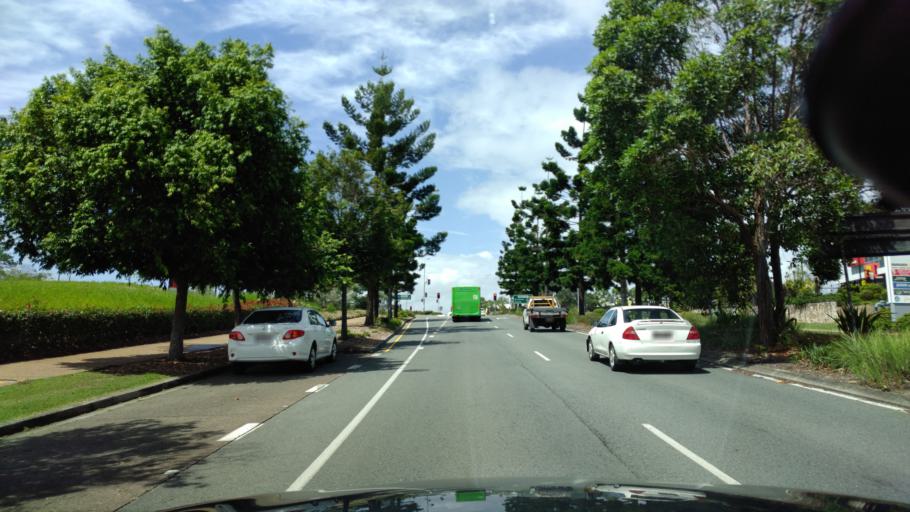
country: AU
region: Queensland
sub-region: Moreton Bay
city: Mango Hill
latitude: -27.2406
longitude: 153.0240
